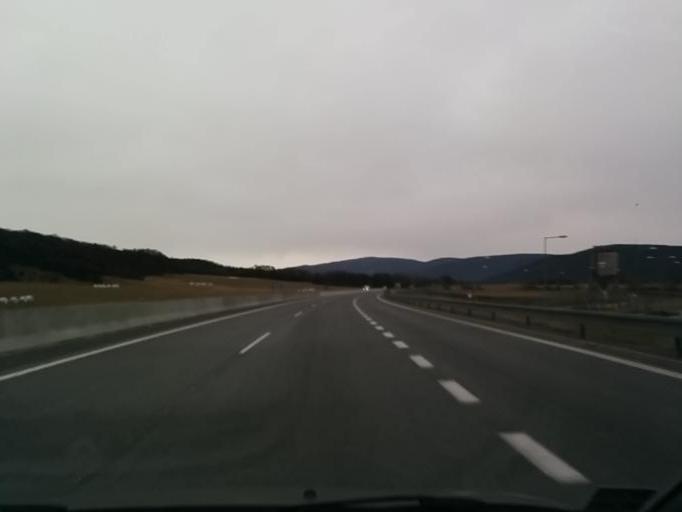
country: SK
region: Nitriansky
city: Tlmace
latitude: 48.3715
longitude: 18.5333
